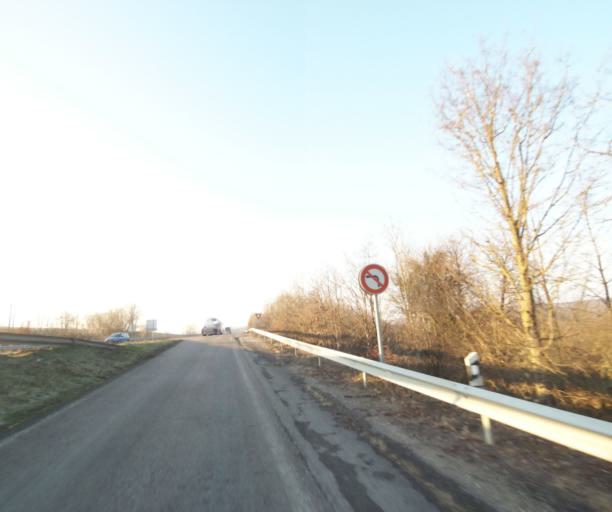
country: FR
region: Champagne-Ardenne
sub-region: Departement de la Haute-Marne
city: Chevillon
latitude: 48.5421
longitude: 5.0842
